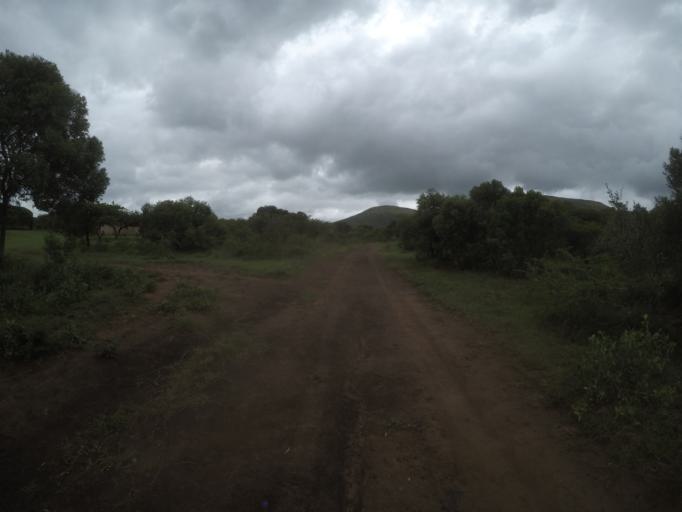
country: ZA
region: KwaZulu-Natal
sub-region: uThungulu District Municipality
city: Empangeni
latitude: -28.5684
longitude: 31.8731
